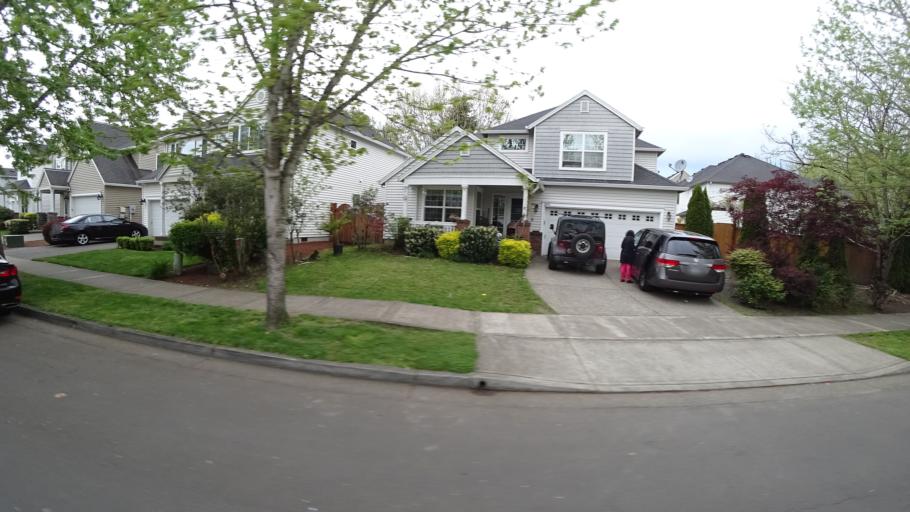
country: US
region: Oregon
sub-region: Washington County
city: Hillsboro
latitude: 45.5428
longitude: -122.9728
